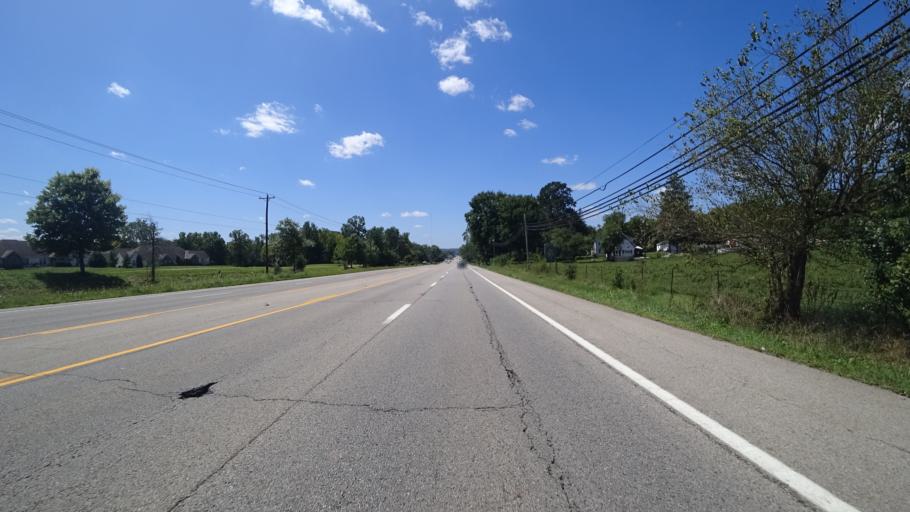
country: US
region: Ohio
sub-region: Butler County
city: New Miami
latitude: 39.4058
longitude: -84.5209
